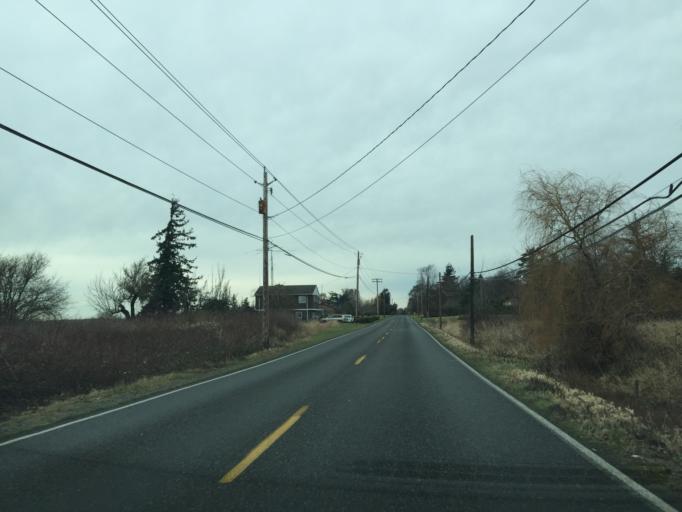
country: US
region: Washington
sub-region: Whatcom County
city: Marietta-Alderwood
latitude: 48.7760
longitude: -122.5334
